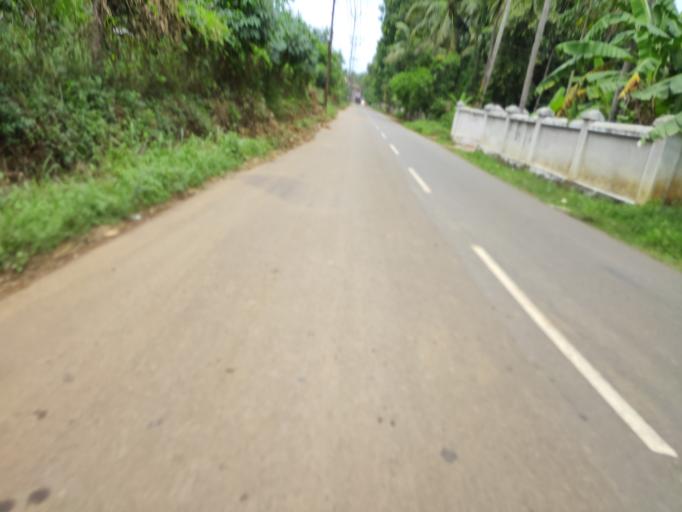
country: IN
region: Kerala
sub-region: Malappuram
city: Manjeri
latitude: 11.2127
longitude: 76.2608
